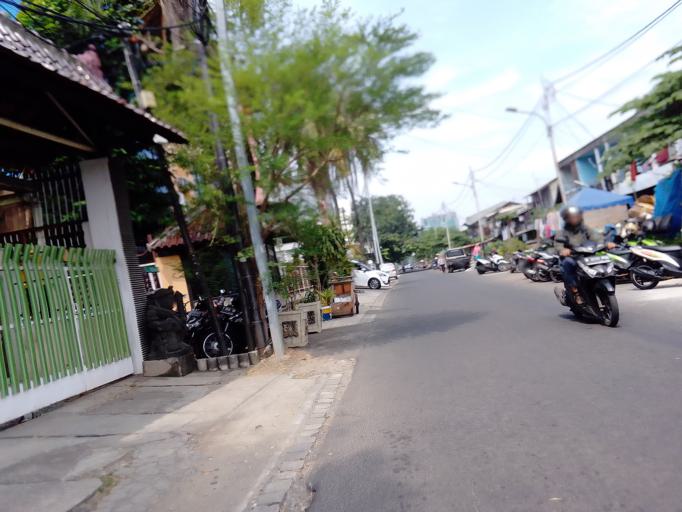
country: ID
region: Jakarta Raya
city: Jakarta
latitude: -6.1747
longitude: 106.8071
